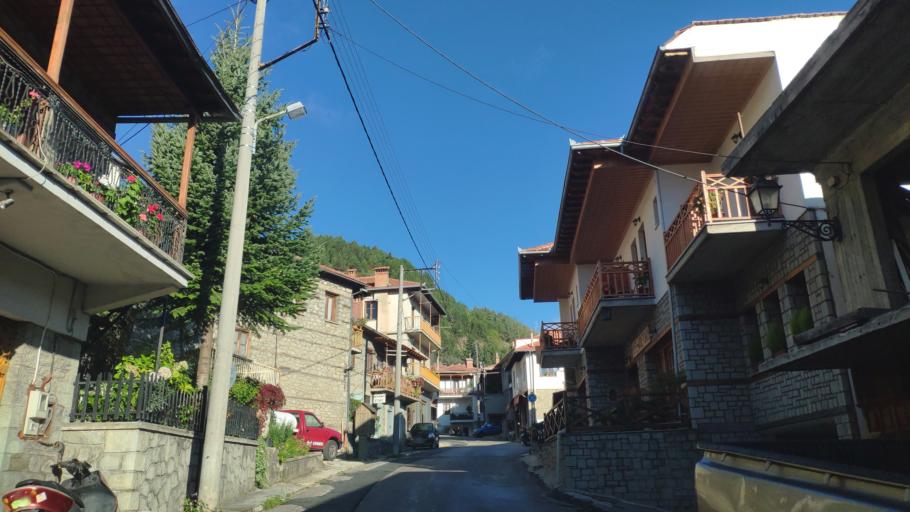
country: GR
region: Epirus
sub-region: Nomos Ioanninon
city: Metsovo
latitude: 39.7723
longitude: 21.1811
